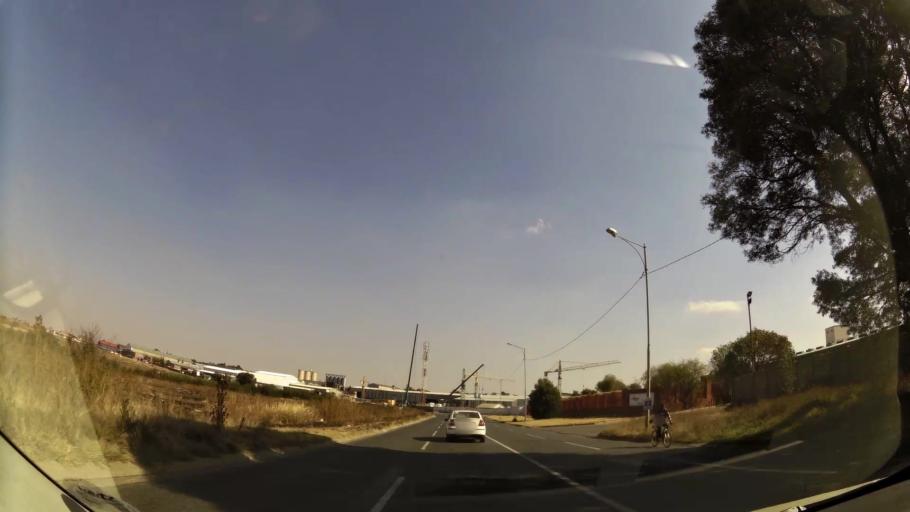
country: ZA
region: Gauteng
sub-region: City of Johannesburg Metropolitan Municipality
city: Roodepoort
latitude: -26.1562
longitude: 27.8063
